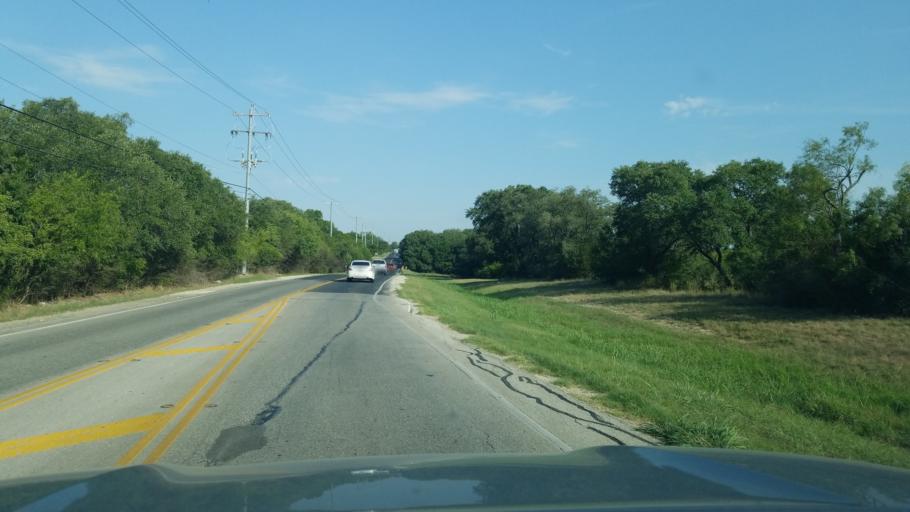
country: US
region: Texas
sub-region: Bexar County
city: Helotes
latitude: 29.4624
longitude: -98.7599
